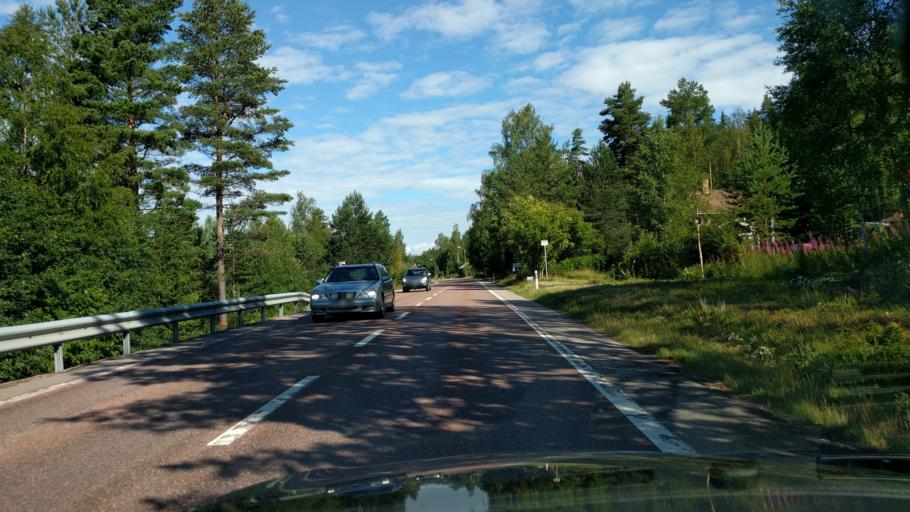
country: SE
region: Dalarna
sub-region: Alvdalens Kommun
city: AElvdalen
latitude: 61.1790
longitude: 14.0980
